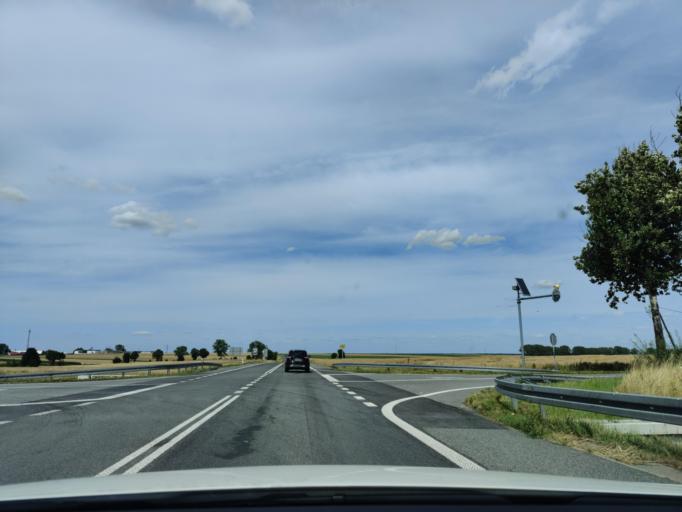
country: PL
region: Opole Voivodeship
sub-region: Powiat prudnicki
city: Biala
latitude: 50.3807
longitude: 17.6747
